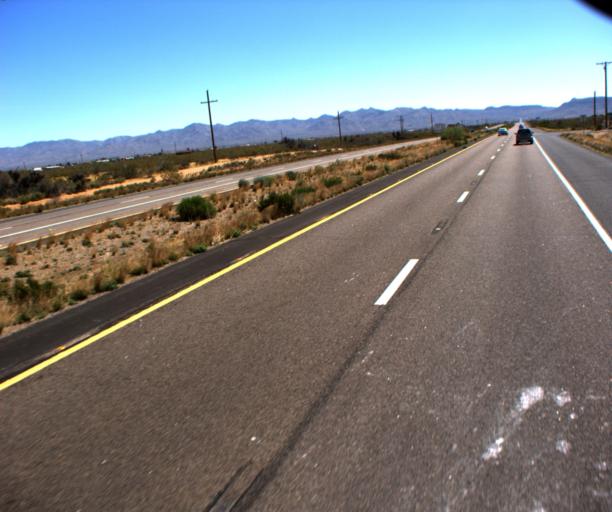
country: US
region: Arizona
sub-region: Mohave County
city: Golden Valley
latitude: 35.2248
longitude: -114.2751
